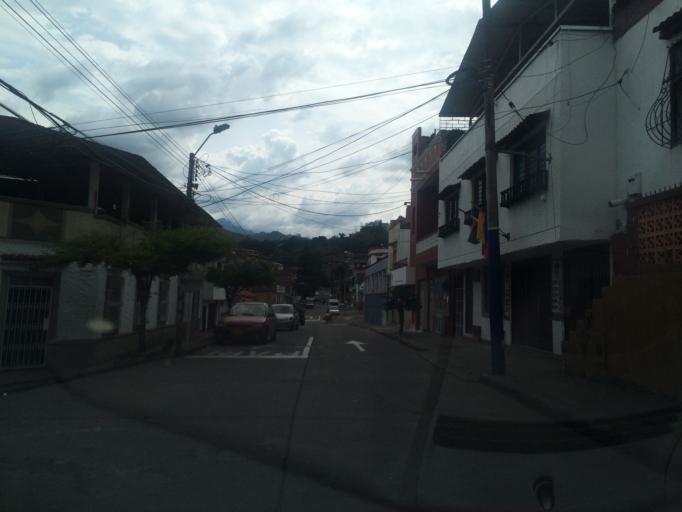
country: CO
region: Valle del Cauca
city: Cali
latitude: 3.4452
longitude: -76.5395
